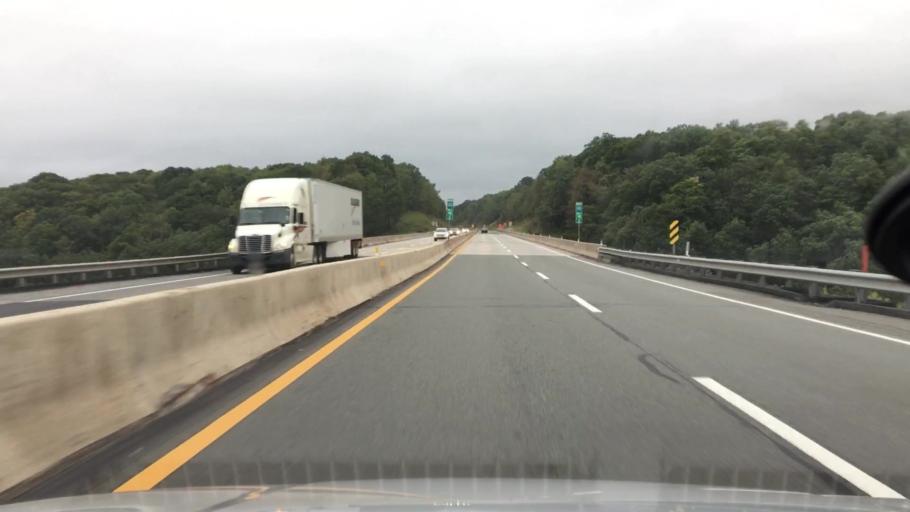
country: US
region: Pennsylvania
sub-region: Luzerne County
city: White Haven
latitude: 41.1032
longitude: -75.7487
